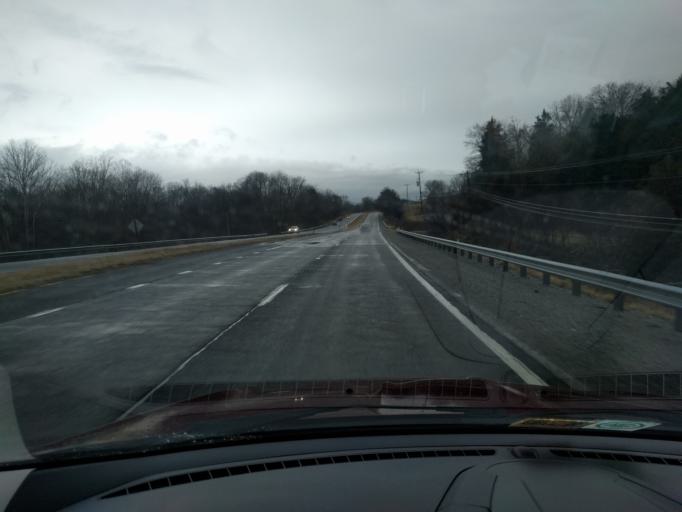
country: US
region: Virginia
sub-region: Giles County
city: Pembroke
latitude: 37.3004
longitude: -80.5607
